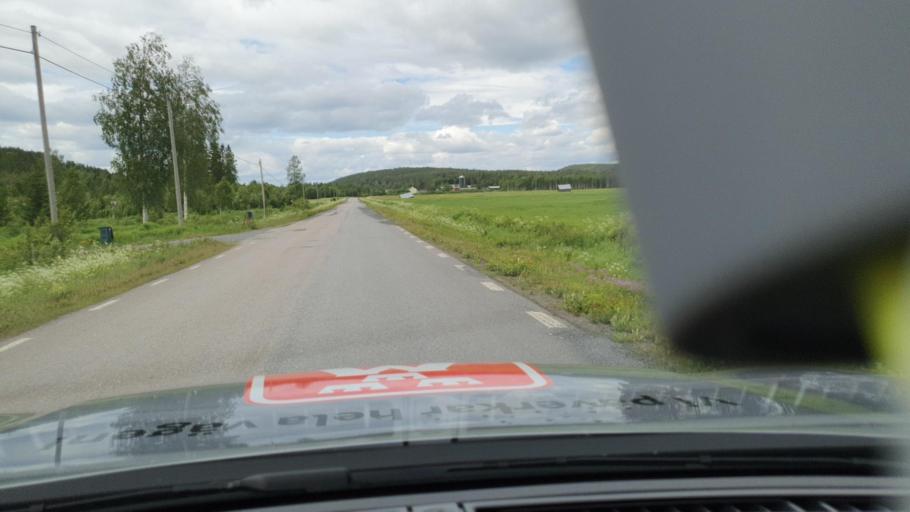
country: SE
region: Norrbotten
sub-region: Bodens Kommun
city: Saevast
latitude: 65.8635
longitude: 21.9079
